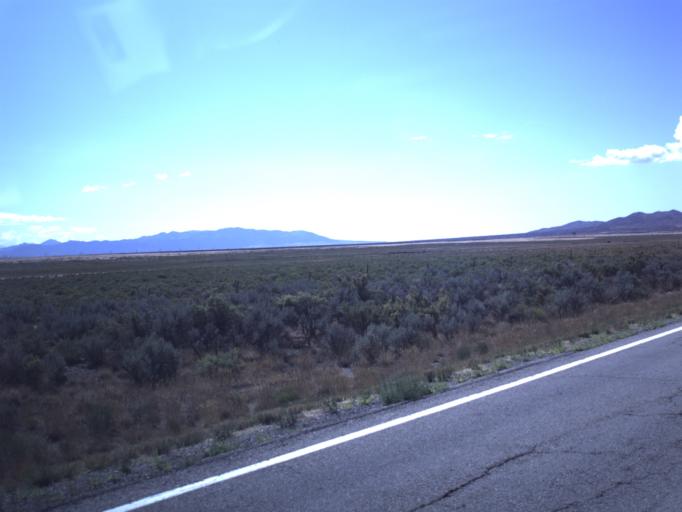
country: US
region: Utah
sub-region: Tooele County
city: Tooele
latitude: 40.2217
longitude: -112.4051
